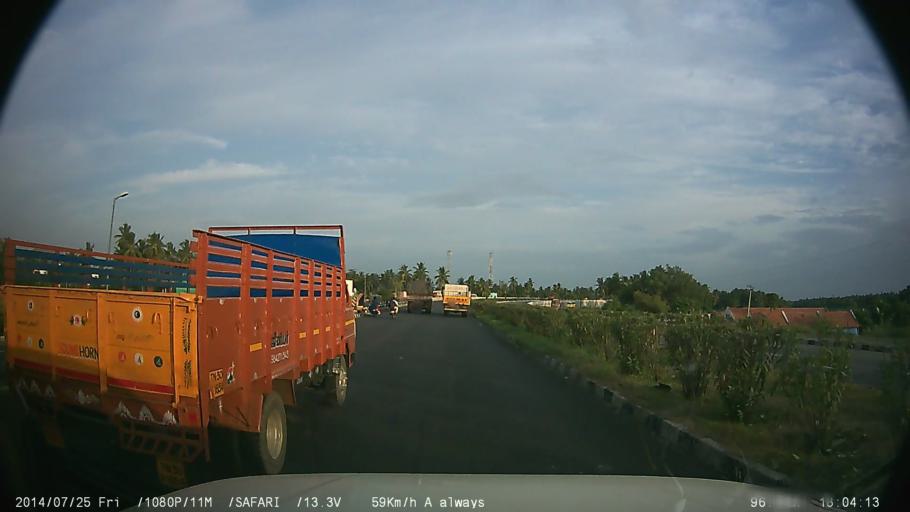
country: IN
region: Tamil Nadu
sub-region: Krishnagiri
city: Kaverippattanam
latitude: 12.4528
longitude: 78.2173
